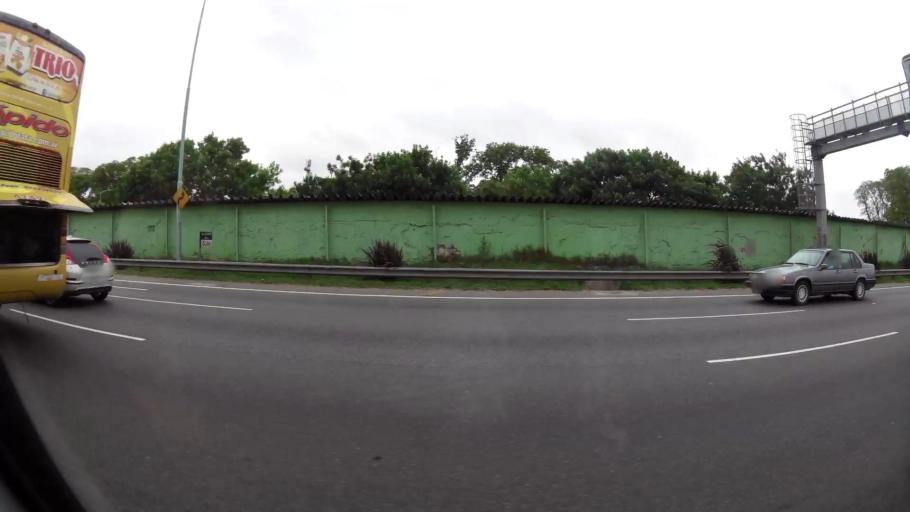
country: AR
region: Buenos Aires F.D.
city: Colegiales
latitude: -34.5585
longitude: -58.4214
